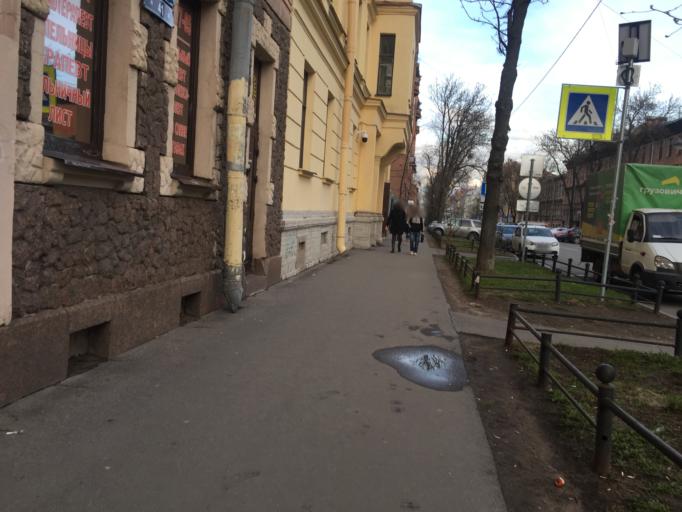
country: RU
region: St.-Petersburg
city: Vasyl'evsky Ostrov
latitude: 59.9454
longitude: 30.2762
